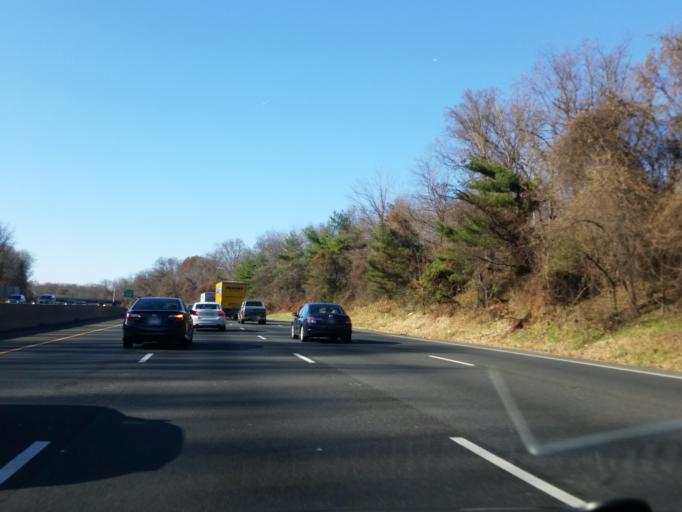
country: US
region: Maryland
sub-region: Montgomery County
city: Cabin John
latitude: 38.9830
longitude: -77.1675
